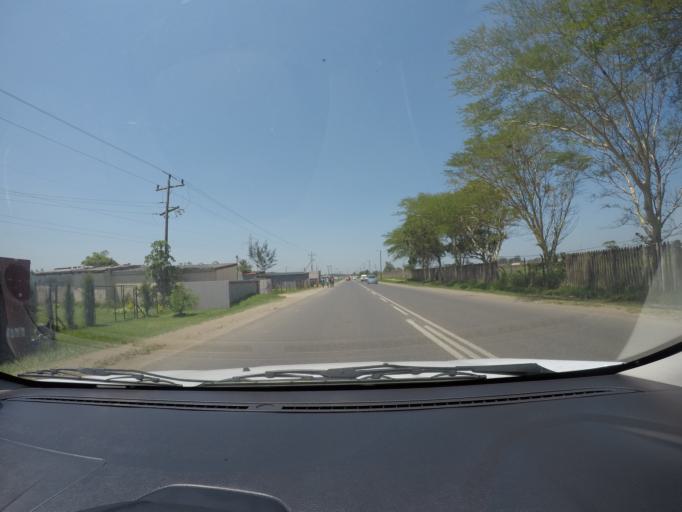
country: ZA
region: KwaZulu-Natal
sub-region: uThungulu District Municipality
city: eSikhawini
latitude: -28.8643
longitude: 31.9107
